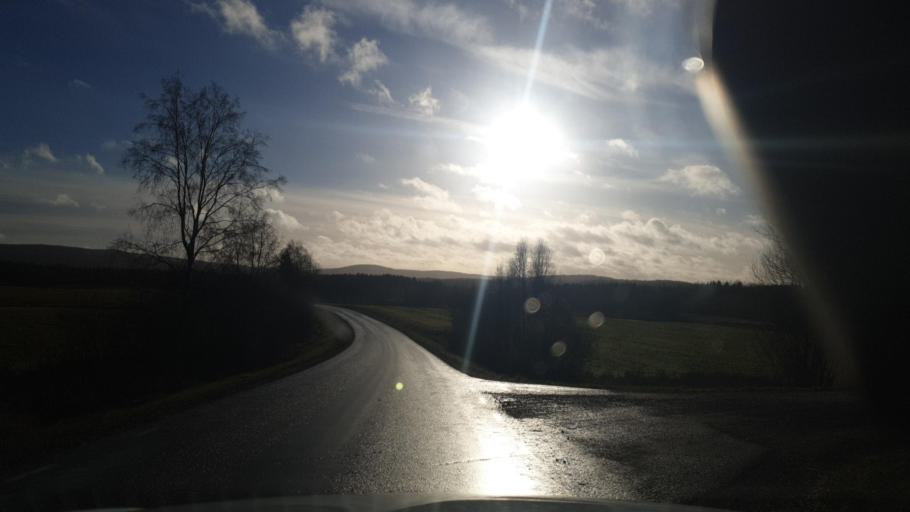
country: SE
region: Vaermland
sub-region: Eda Kommun
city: Charlottenberg
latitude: 59.7843
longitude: 12.1599
